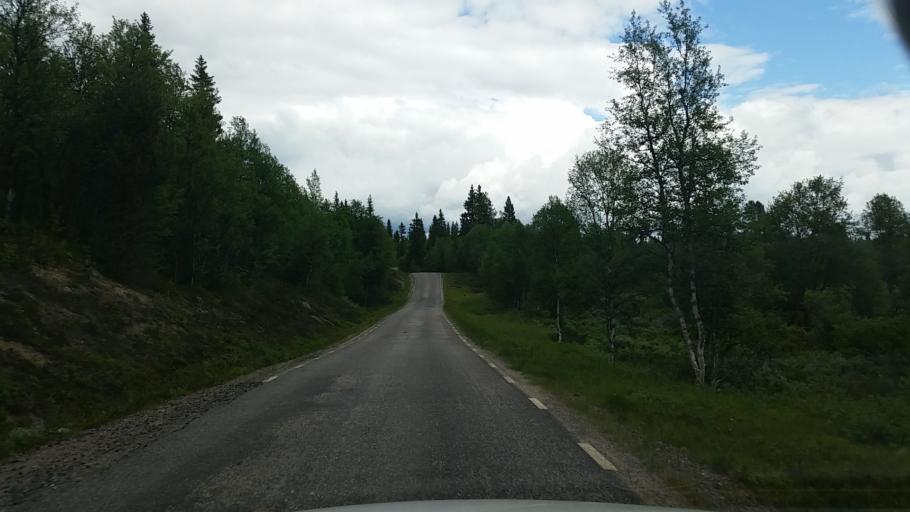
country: NO
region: Hedmark
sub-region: Engerdal
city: Engerdal
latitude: 62.1480
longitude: 12.9913
